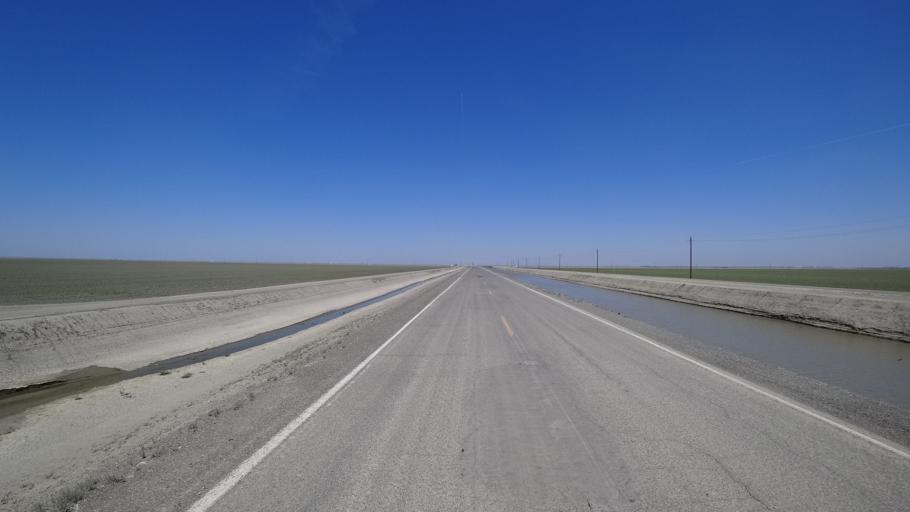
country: US
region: California
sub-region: Kings County
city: Corcoran
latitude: 36.0145
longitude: -119.6432
